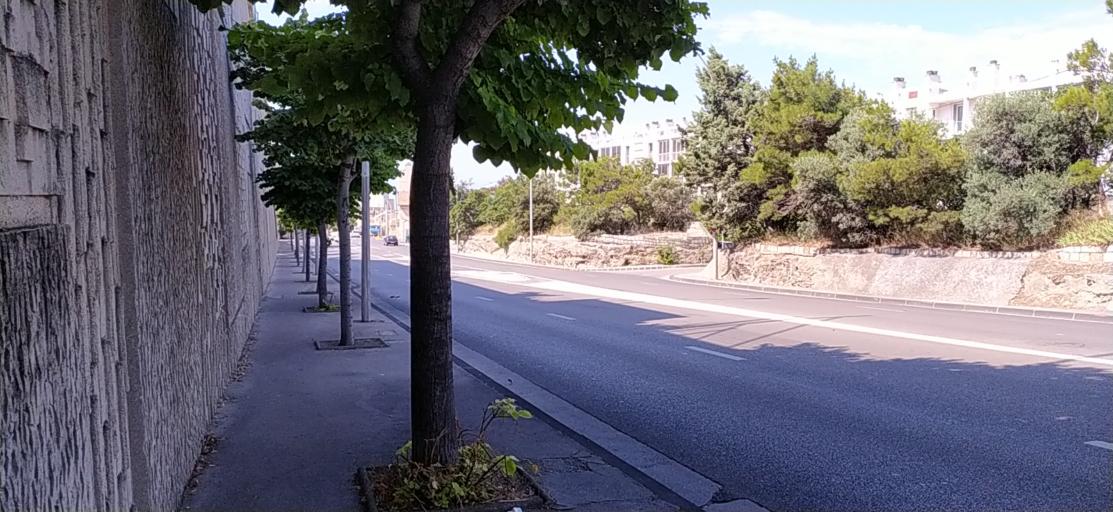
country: FR
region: Provence-Alpes-Cote d'Azur
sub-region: Departement des Bouches-du-Rhone
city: Marseille 16
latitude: 43.3435
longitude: 5.3535
